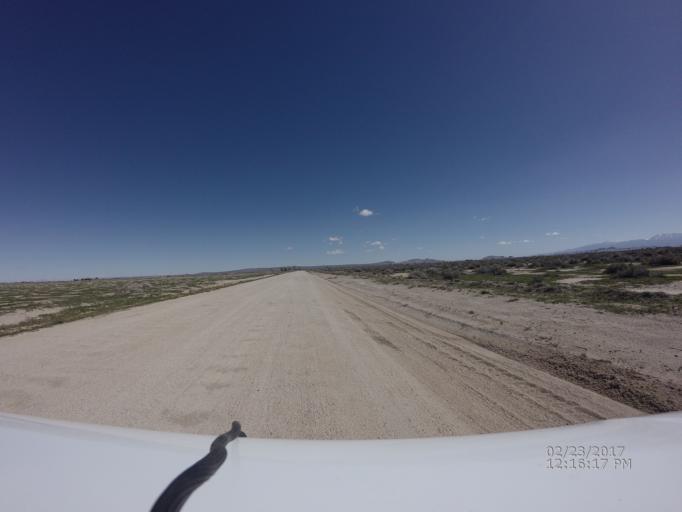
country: US
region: California
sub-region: Los Angeles County
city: Lancaster
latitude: 34.7415
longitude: -117.9852
